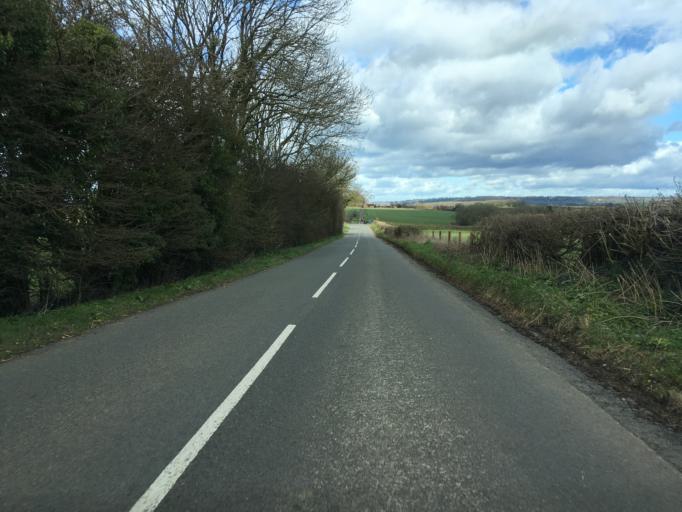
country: GB
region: England
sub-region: South Gloucestershire
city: Horton
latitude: 51.5890
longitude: -2.3314
